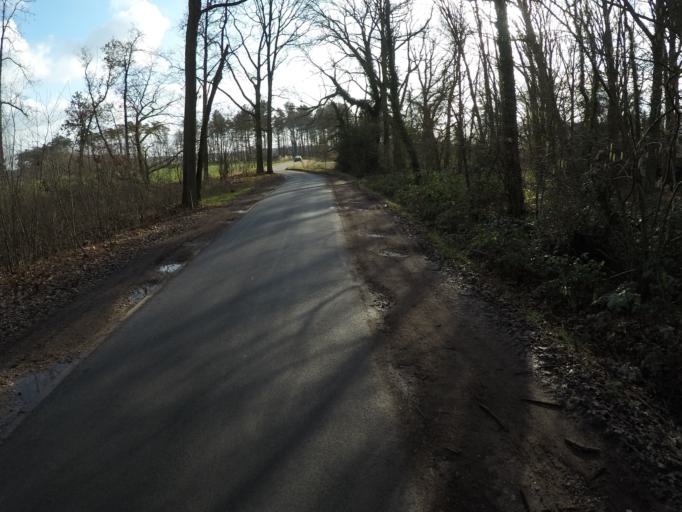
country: BE
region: Flanders
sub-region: Provincie Antwerpen
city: Zoersel
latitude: 51.2430
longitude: 4.7475
